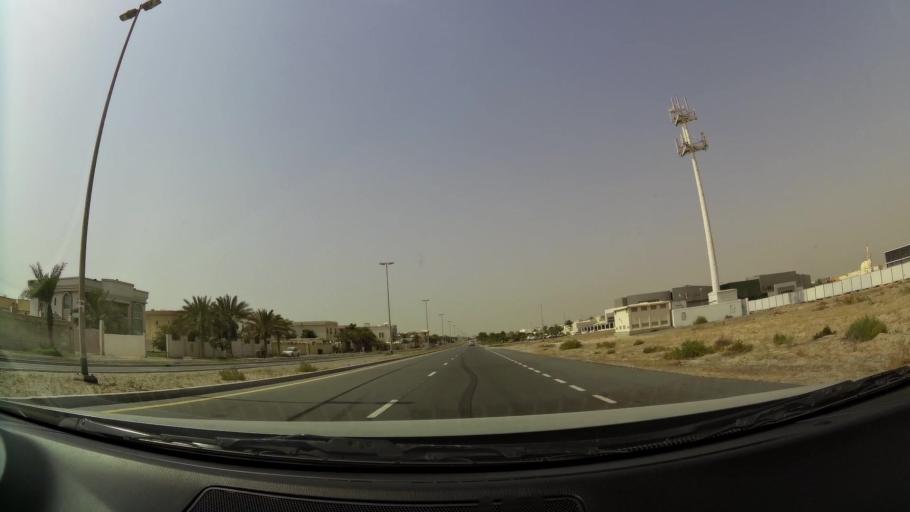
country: AE
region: Ash Shariqah
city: Sharjah
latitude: 25.2437
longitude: 55.4495
